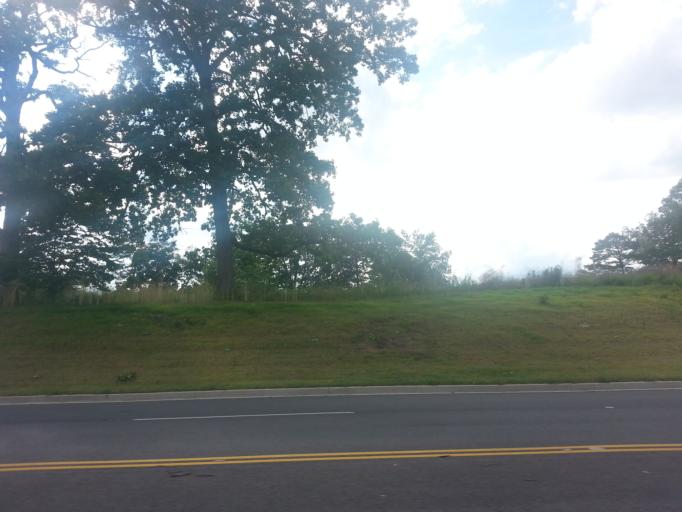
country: US
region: Tennessee
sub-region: Blount County
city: Eagleton Village
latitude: 35.8074
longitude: -83.9393
